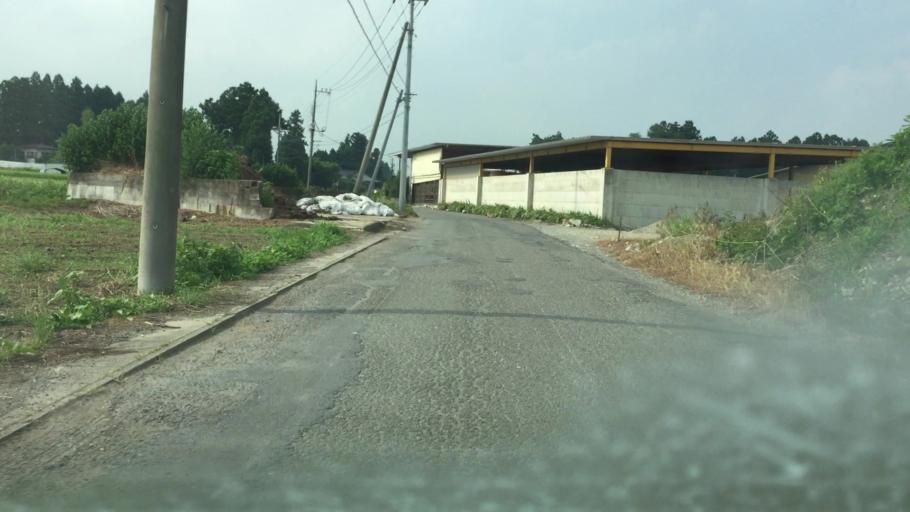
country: JP
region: Tochigi
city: Kuroiso
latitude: 36.9696
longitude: 139.9562
